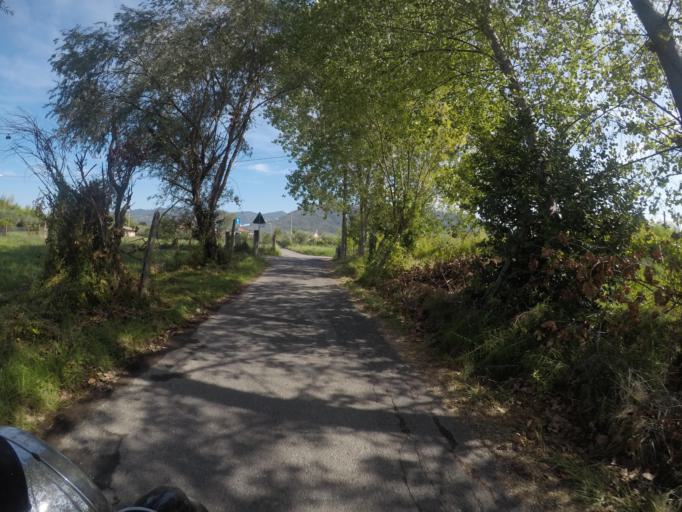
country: IT
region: Liguria
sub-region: Provincia di La Spezia
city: Casano-Dogana-Isola
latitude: 44.0599
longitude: 10.0333
